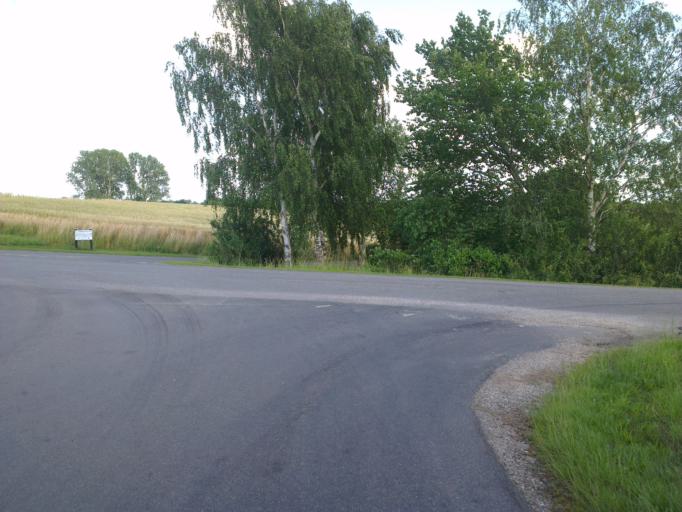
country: DK
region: Capital Region
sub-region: Frederikssund Kommune
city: Skibby
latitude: 55.7520
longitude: 12.0342
